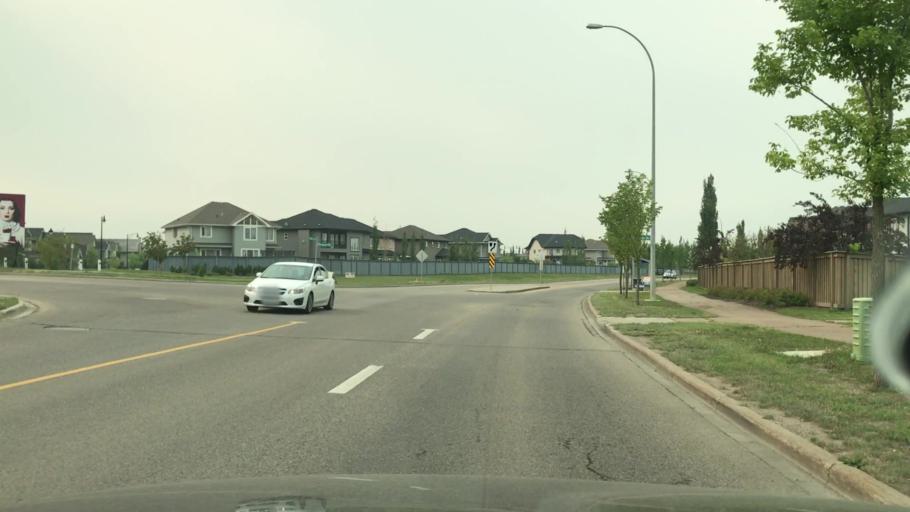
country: CA
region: Alberta
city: Edmonton
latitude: 53.4394
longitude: -113.5659
